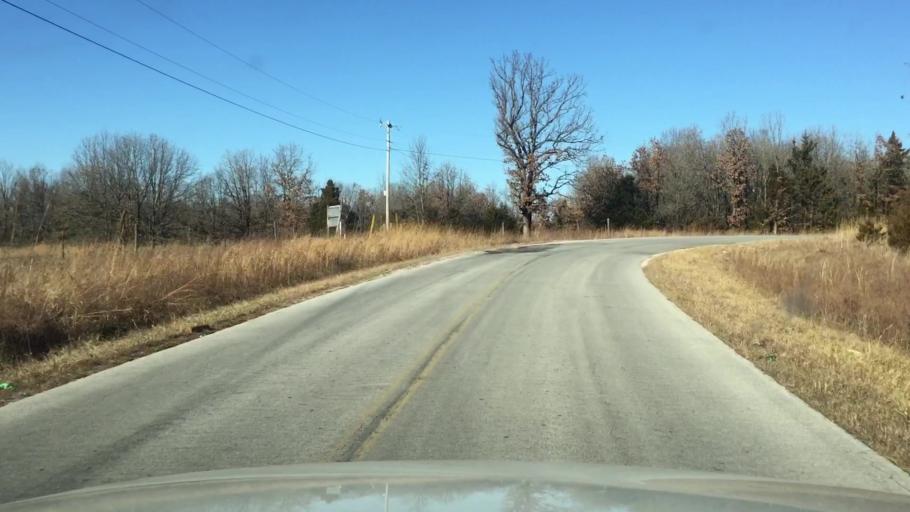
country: US
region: Missouri
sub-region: Morgan County
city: Versailles
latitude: 38.3486
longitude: -92.7490
